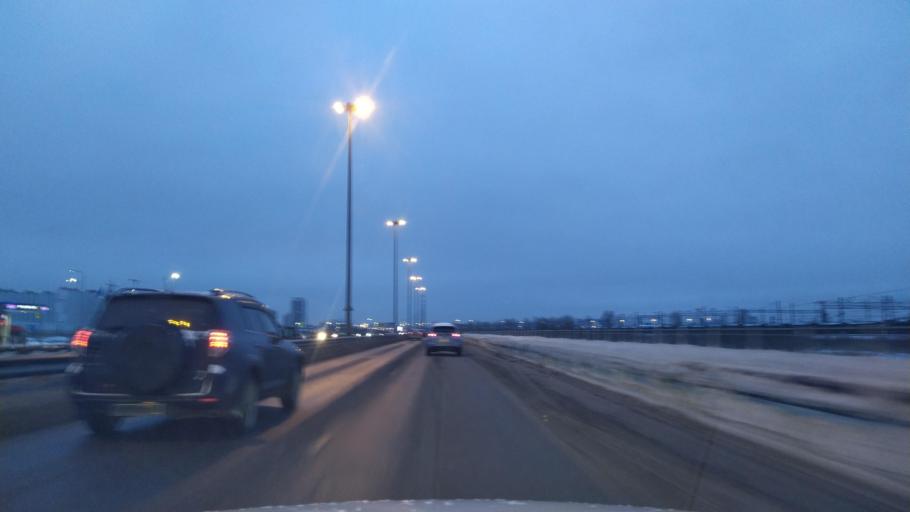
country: RU
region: St.-Petersburg
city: Shushary
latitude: 59.7933
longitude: 30.3914
